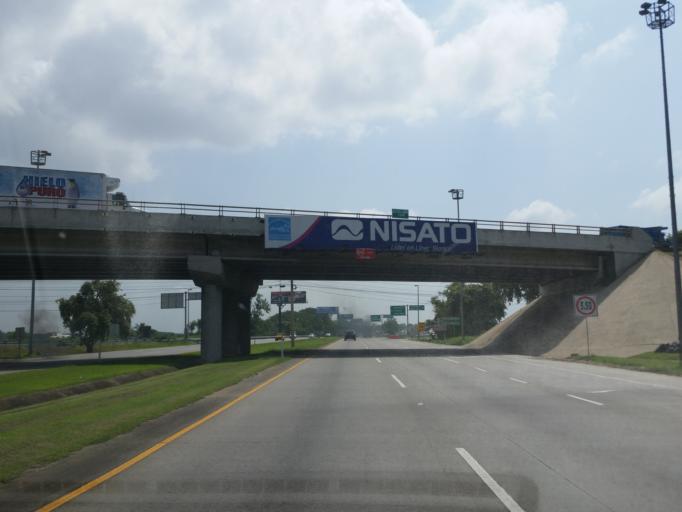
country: PA
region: Panama
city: San Miguelito
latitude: 9.0291
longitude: -79.4557
